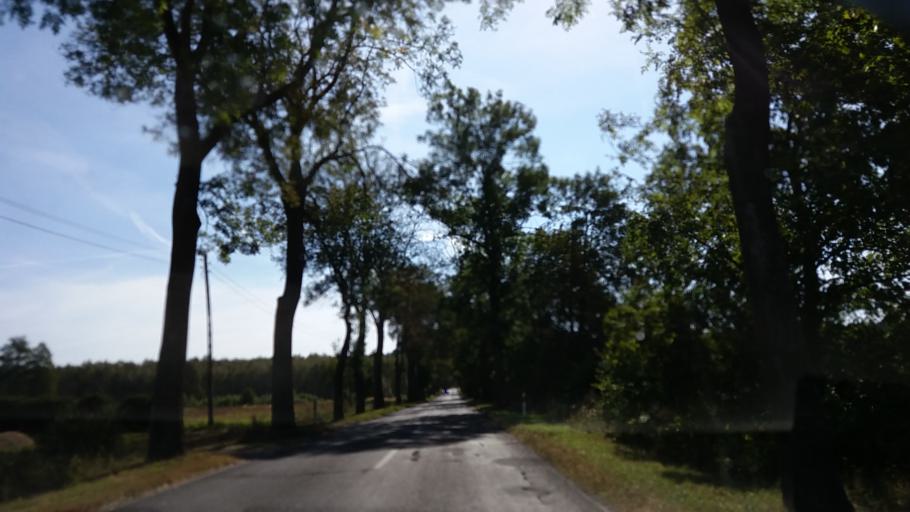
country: PL
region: Lubusz
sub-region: Powiat strzelecko-drezdenecki
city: Drezdenko
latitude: 52.7444
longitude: 15.8583
